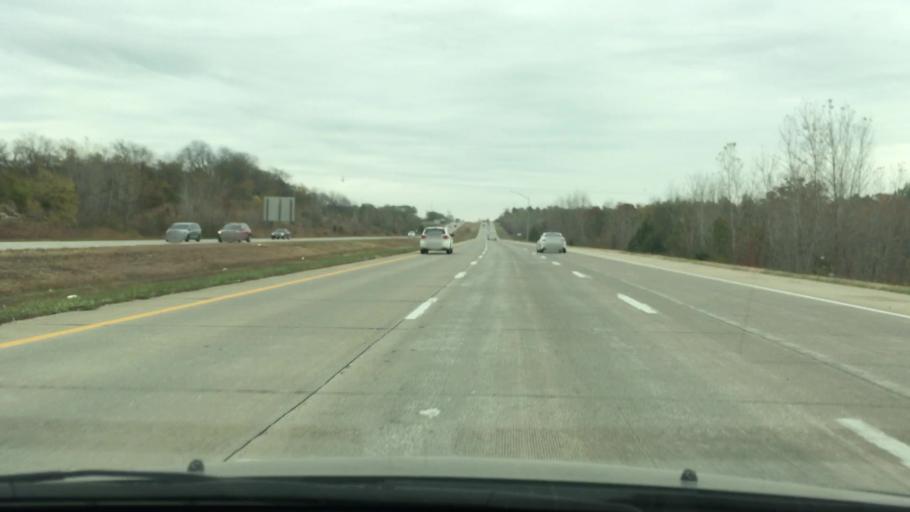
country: US
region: Missouri
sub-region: Jackson County
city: Grandview
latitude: 38.8612
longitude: -94.5801
